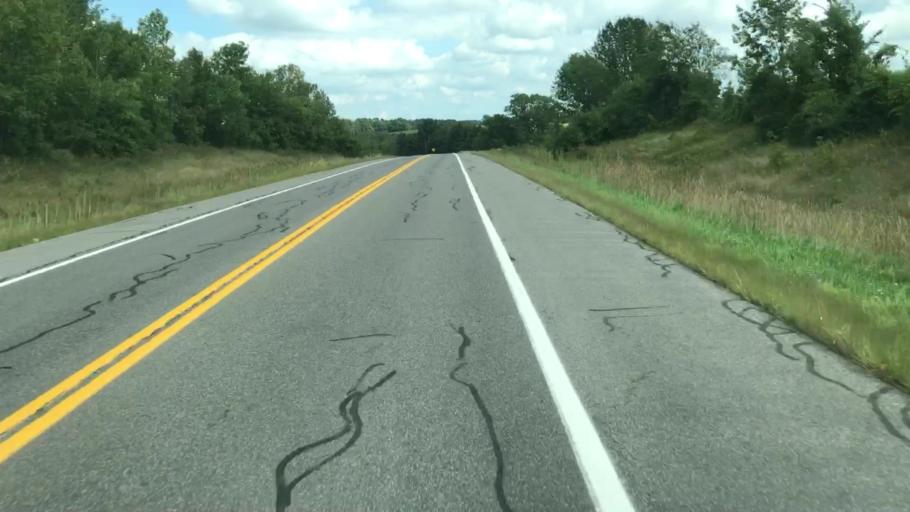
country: US
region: New York
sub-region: Onondaga County
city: Skaneateles
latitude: 42.9479
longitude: -76.3789
